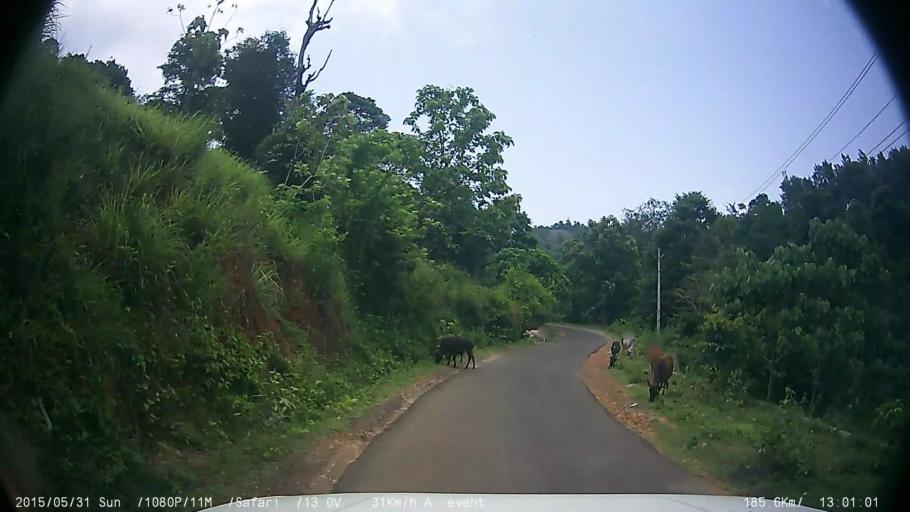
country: IN
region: Kerala
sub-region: Wayanad
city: Kalpetta
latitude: 11.5168
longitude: 76.1346
